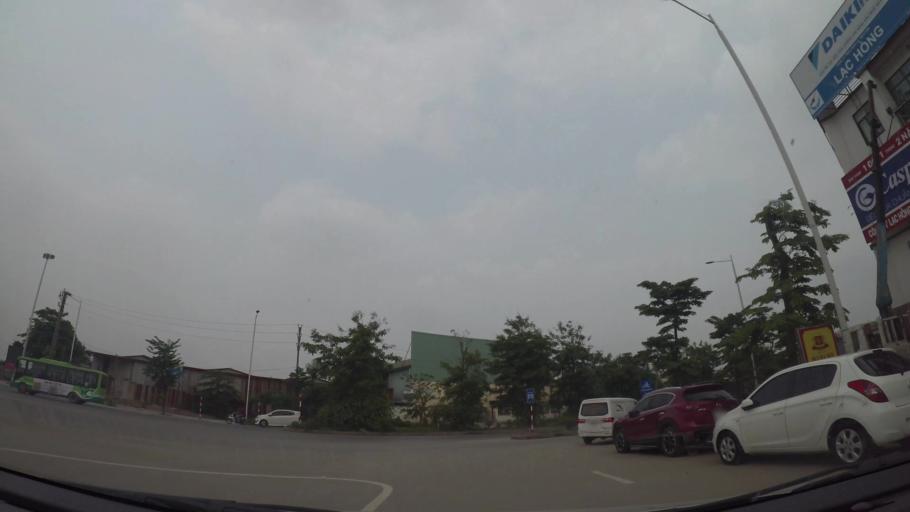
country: VN
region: Ha Noi
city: Cau Dien
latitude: 21.0408
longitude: 105.7382
